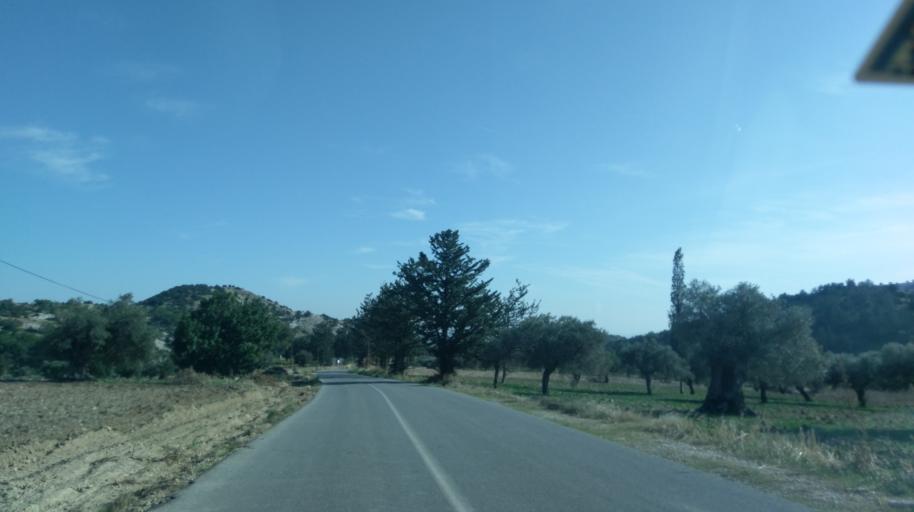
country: CY
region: Ammochostos
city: Trikomo
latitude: 35.3388
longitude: 33.8050
